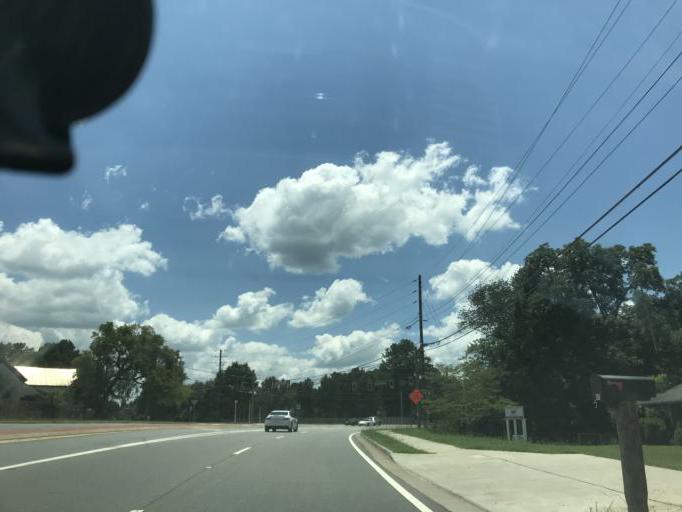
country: US
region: Georgia
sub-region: Fulton County
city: Milton
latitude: 34.1335
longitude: -84.2267
